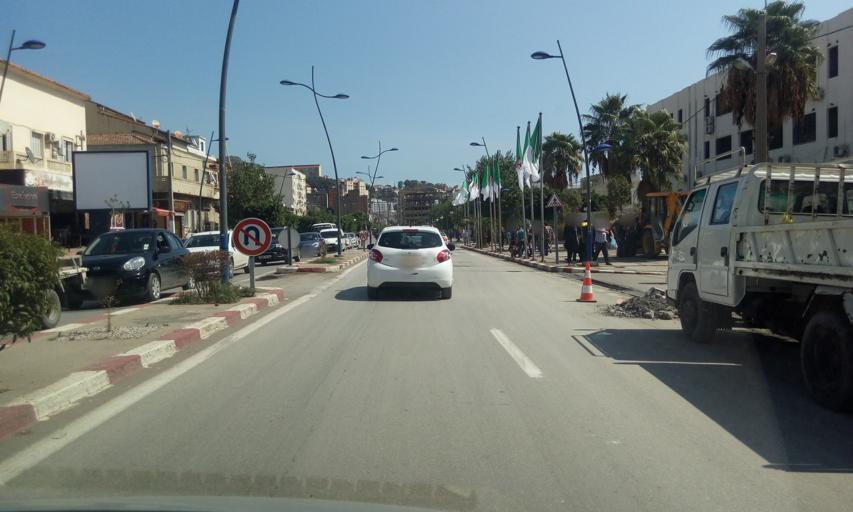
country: DZ
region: Bejaia
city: Bejaia
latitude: 36.7515
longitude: 5.0670
